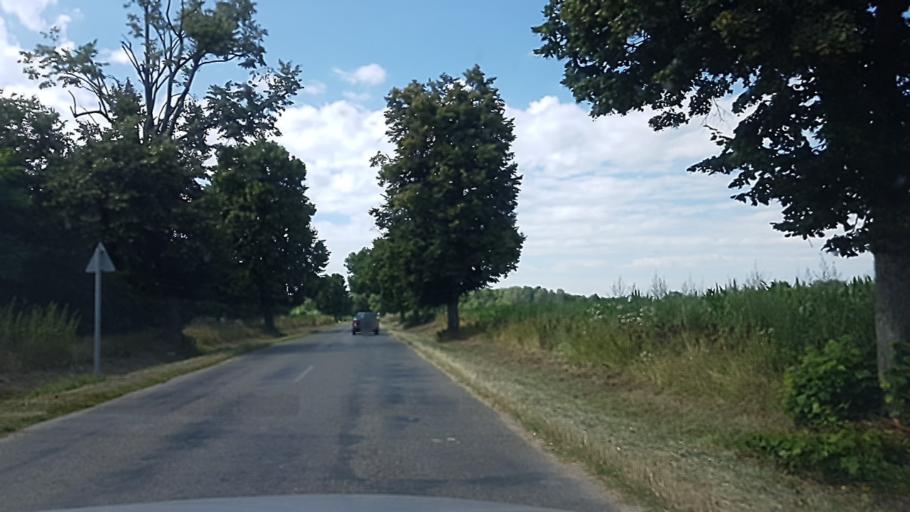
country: HU
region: Somogy
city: Barcs
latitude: 45.9559
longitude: 17.5989
